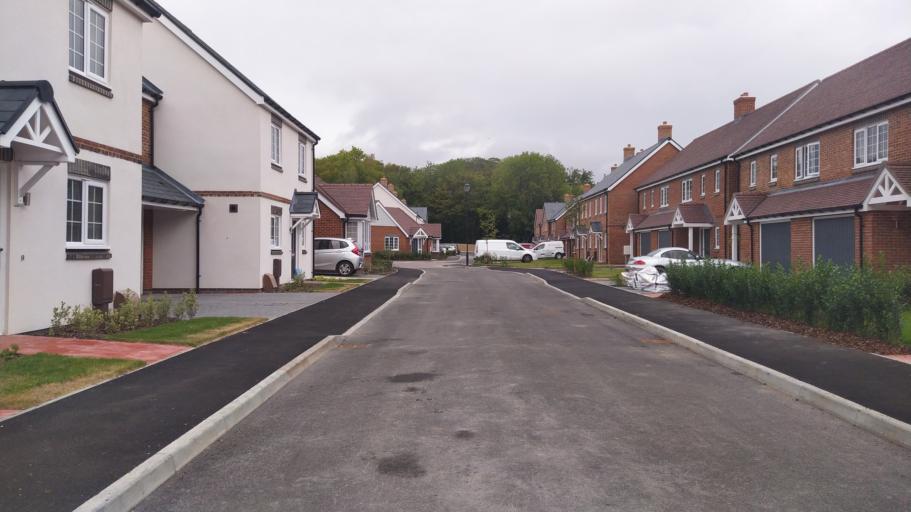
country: GB
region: England
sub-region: Hampshire
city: Havant
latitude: 50.8885
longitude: -0.9591
